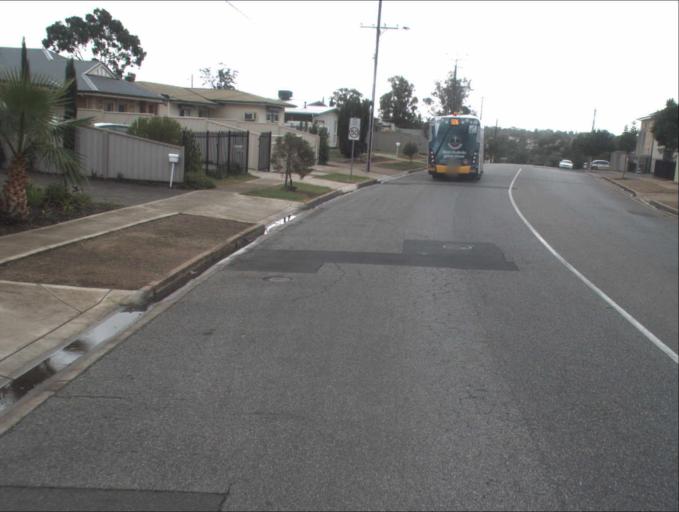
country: AU
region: South Australia
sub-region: Port Adelaide Enfield
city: Gilles Plains
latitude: -34.8480
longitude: 138.6599
